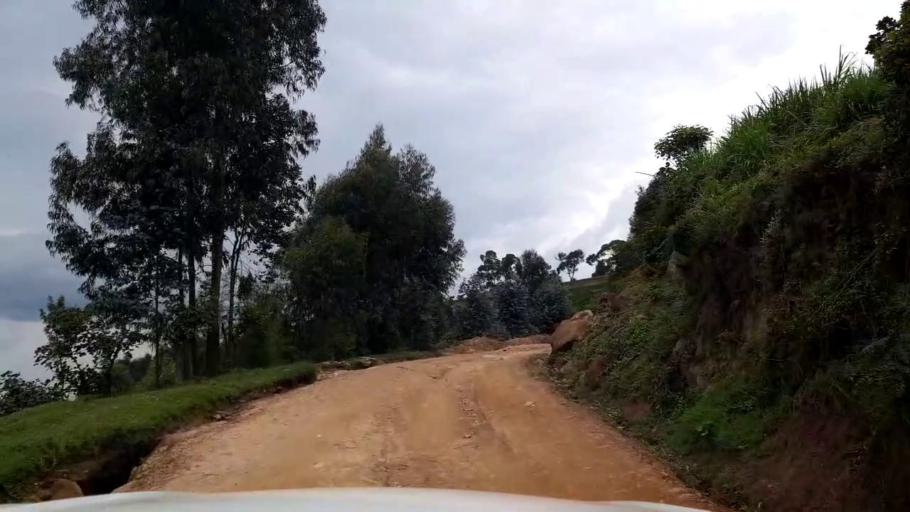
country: RW
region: Western Province
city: Kibuye
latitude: -1.9639
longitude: 29.3945
